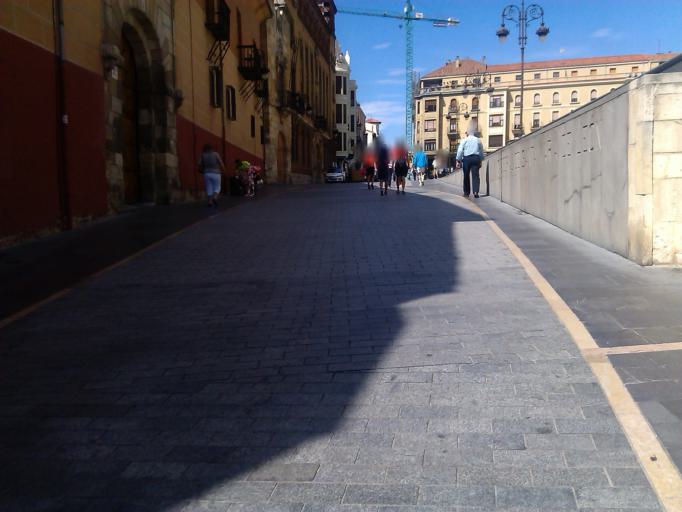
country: ES
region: Castille and Leon
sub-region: Provincia de Leon
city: Leon
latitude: 42.5990
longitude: -5.5662
